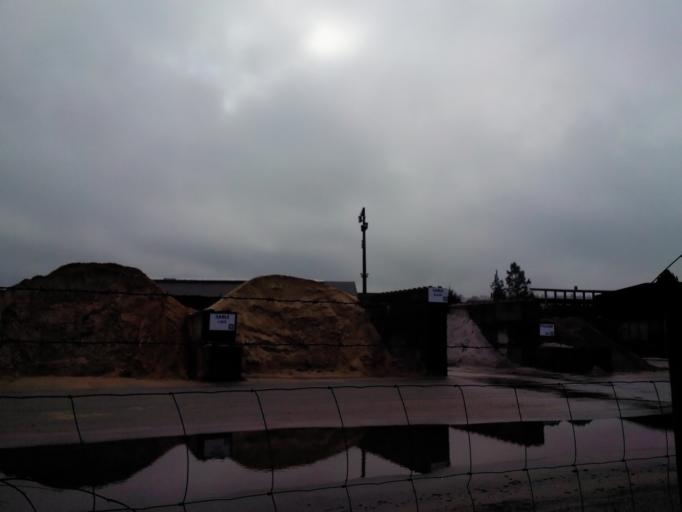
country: BE
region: Wallonia
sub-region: Province du Brabant Wallon
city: Grez-Doiceau
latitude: 50.7379
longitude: 4.6532
